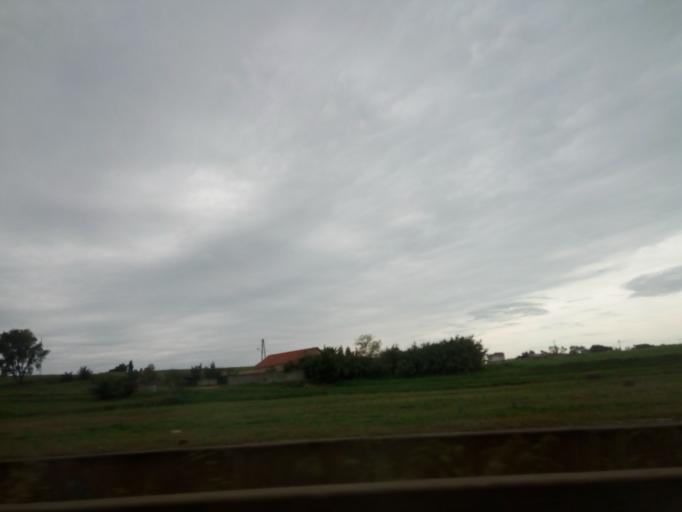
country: DZ
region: Tipaza
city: Cheraga
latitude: 36.7248
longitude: 2.9401
